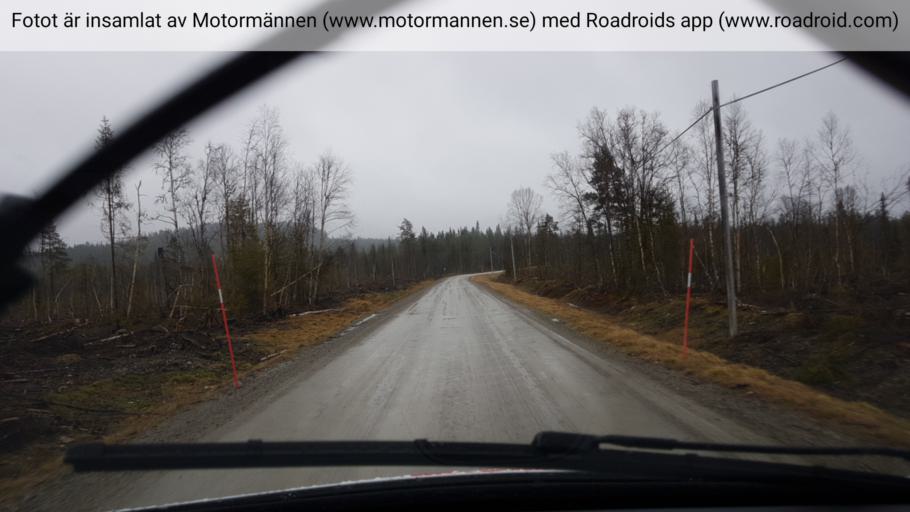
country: SE
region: Jaemtland
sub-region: Are Kommun
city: Jarpen
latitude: 62.6095
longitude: 13.2067
